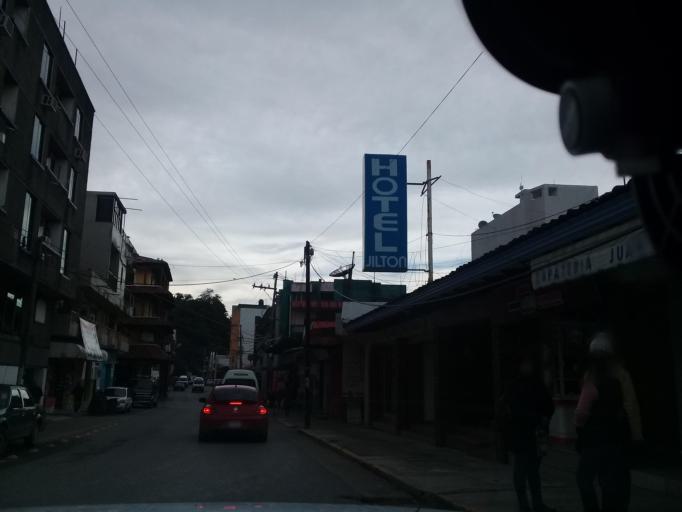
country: MX
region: Hidalgo
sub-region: Huejutla de Reyes
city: Huejutla de Reyes
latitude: 21.1424
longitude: -98.4192
